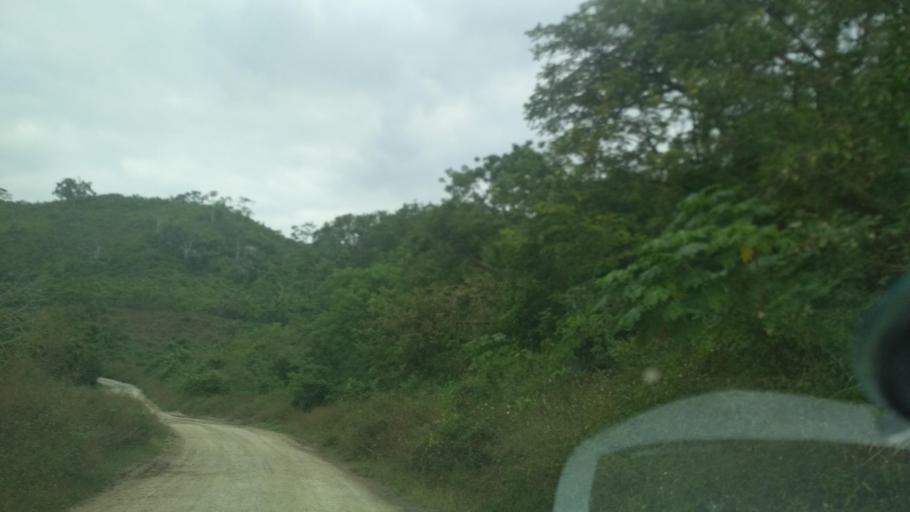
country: MX
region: Veracruz
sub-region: Poza Rica de Hidalgo
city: El Mollejon
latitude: 20.5246
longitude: -97.3886
